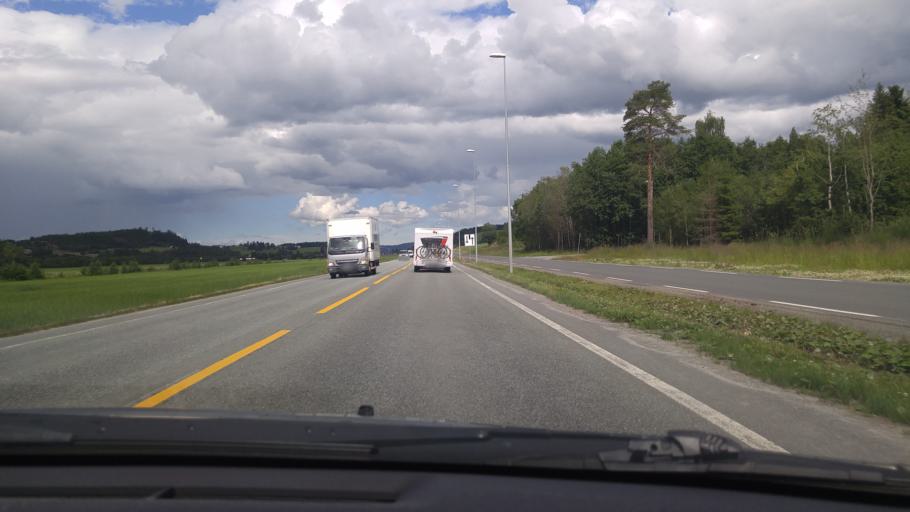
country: NO
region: Nord-Trondelag
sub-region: Steinkjer
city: Steinkjer
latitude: 63.9396
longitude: 11.4210
